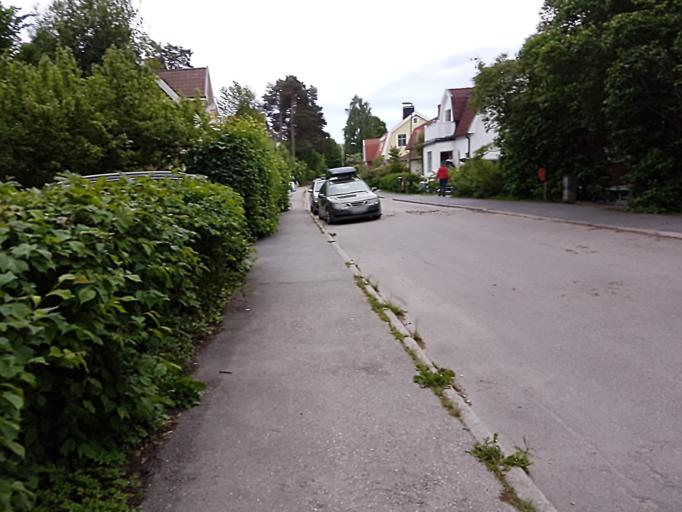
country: SE
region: Stockholm
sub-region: Stockholms Kommun
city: Arsta
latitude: 59.2865
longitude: 18.0812
